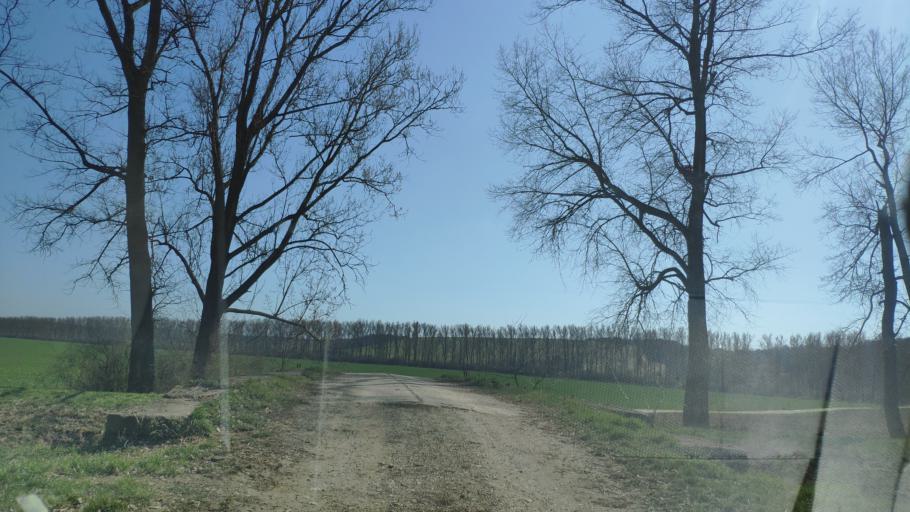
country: SK
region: Kosicky
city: Moldava nad Bodvou
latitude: 48.5723
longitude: 20.9464
